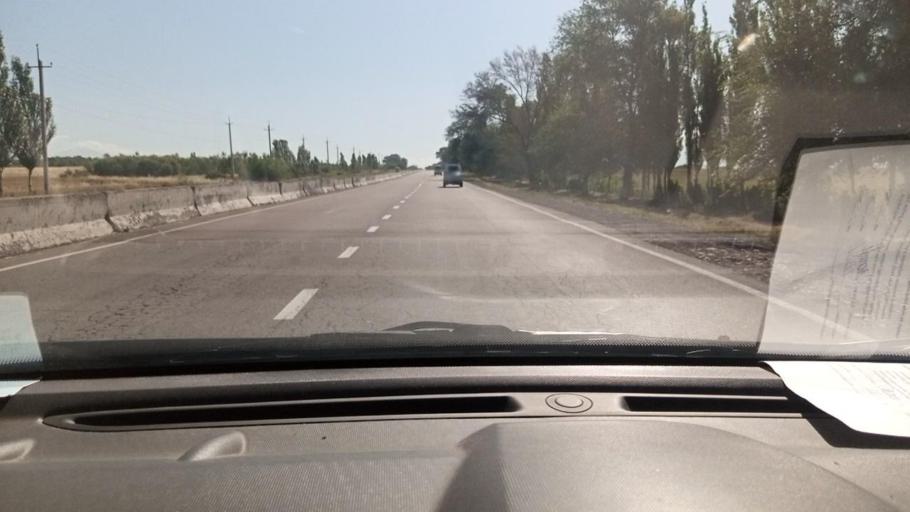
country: UZ
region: Toshkent
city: Ohangaron
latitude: 40.9316
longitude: 69.8749
